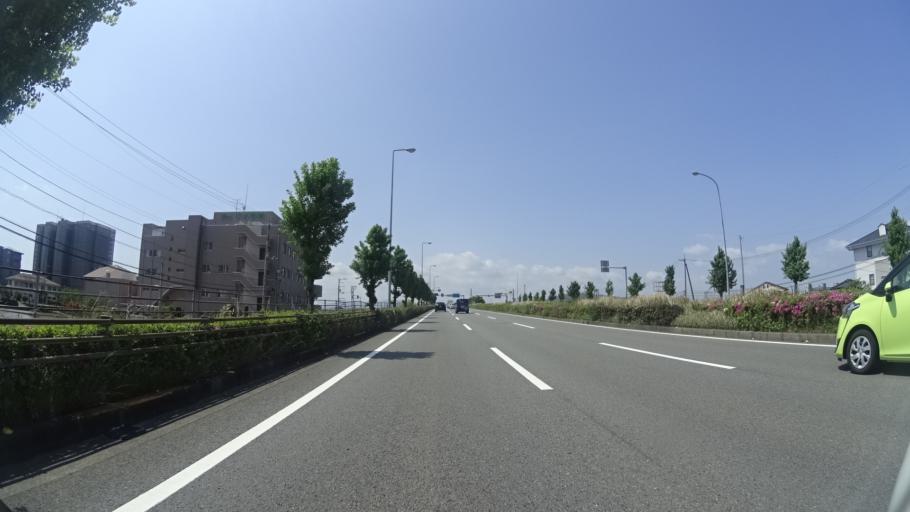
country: JP
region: Tokushima
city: Tokushima-shi
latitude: 34.0958
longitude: 134.5723
